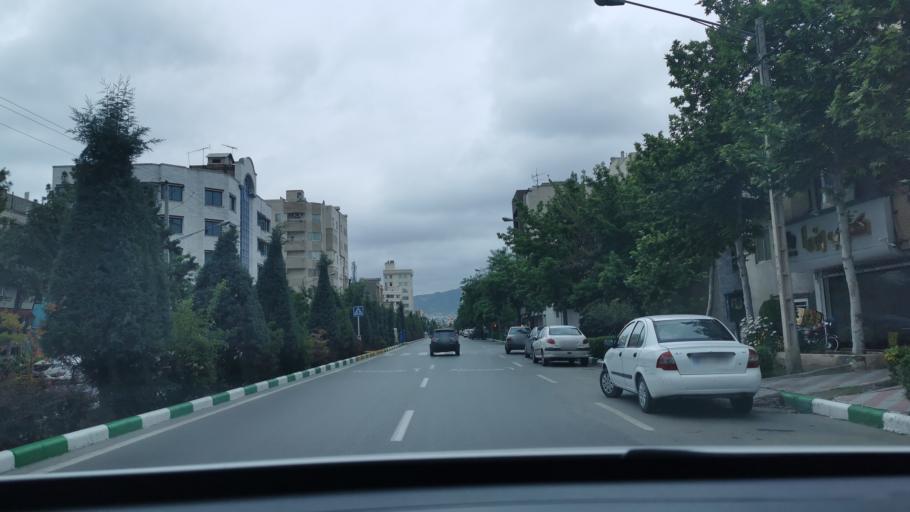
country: IR
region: Razavi Khorasan
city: Mashhad
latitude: 36.3271
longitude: 59.5278
